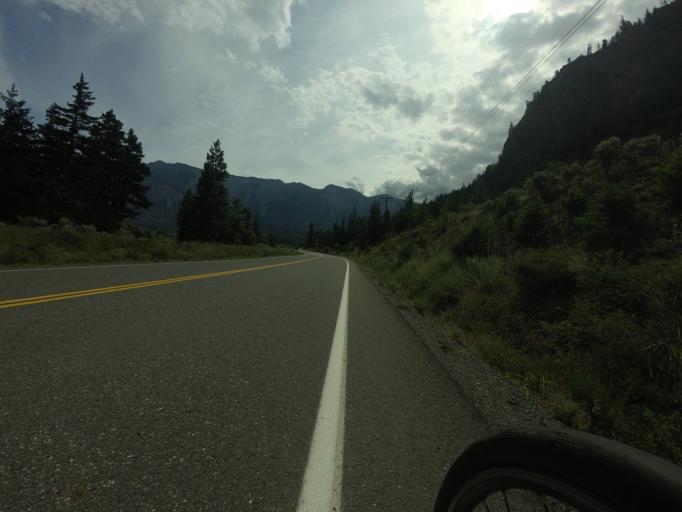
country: CA
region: British Columbia
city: Lillooet
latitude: 50.6703
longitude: -121.9515
